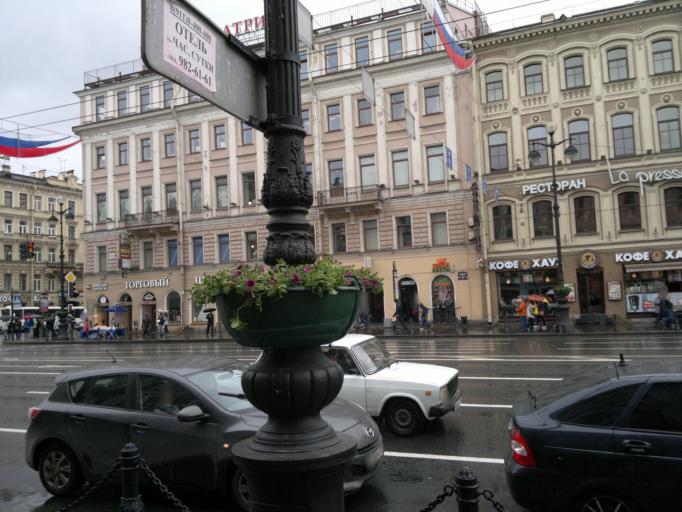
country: RU
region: St.-Petersburg
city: Centralniy
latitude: 59.9320
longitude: 30.3546
